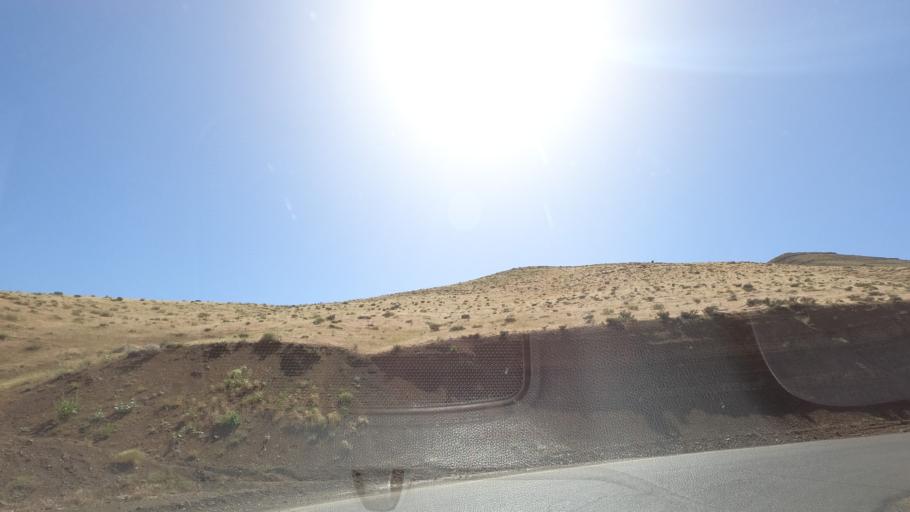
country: IR
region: Alborz
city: Karaj
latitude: 35.9389
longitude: 51.0796
